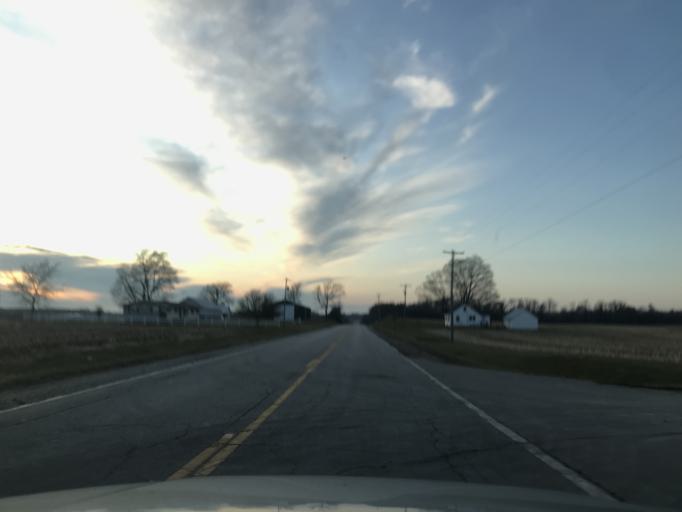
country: US
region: Illinois
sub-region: Henderson County
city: Oquawka
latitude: 41.0185
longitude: -90.7999
